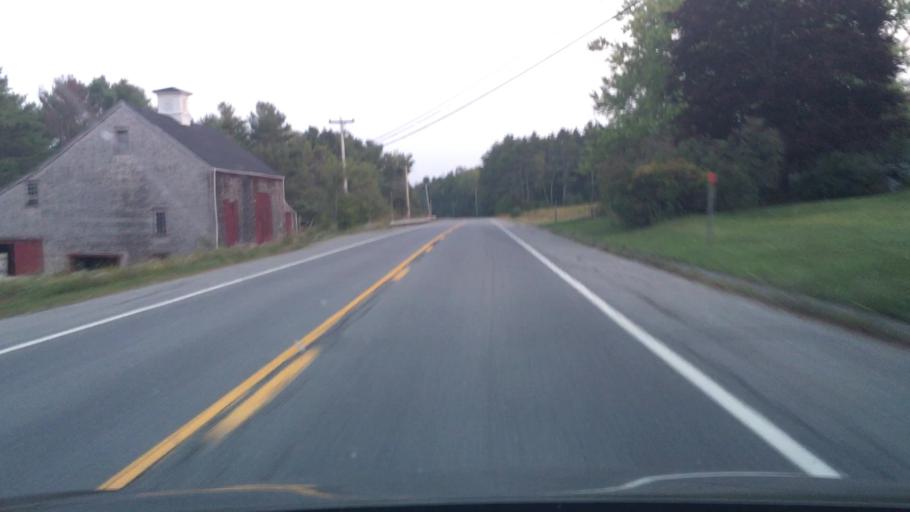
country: US
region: Maine
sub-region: Waldo County
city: Stockton Springs
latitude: 44.5474
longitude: -68.8642
